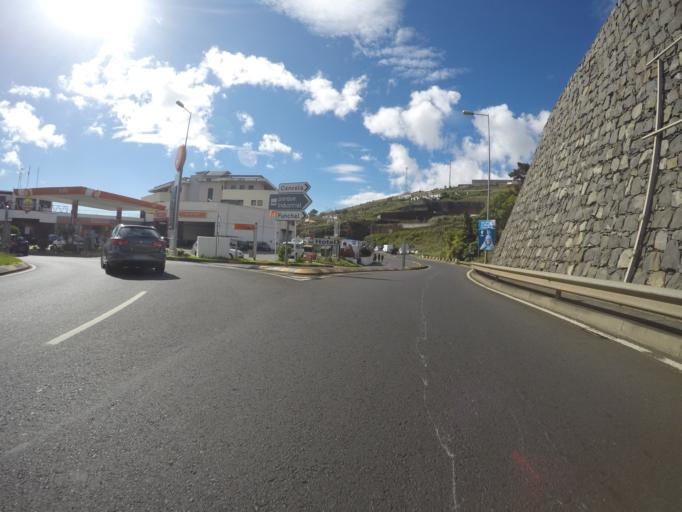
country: PT
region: Madeira
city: Canico
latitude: 32.6485
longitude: -16.8589
